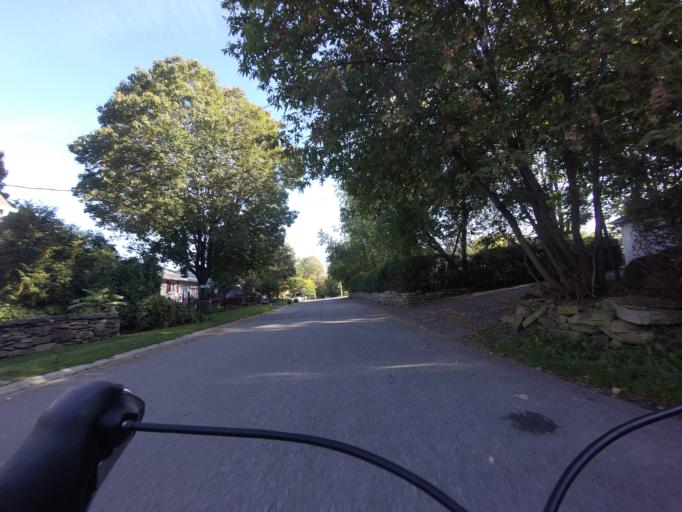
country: CA
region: Ontario
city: Bells Corners
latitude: 45.2251
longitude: -75.6818
